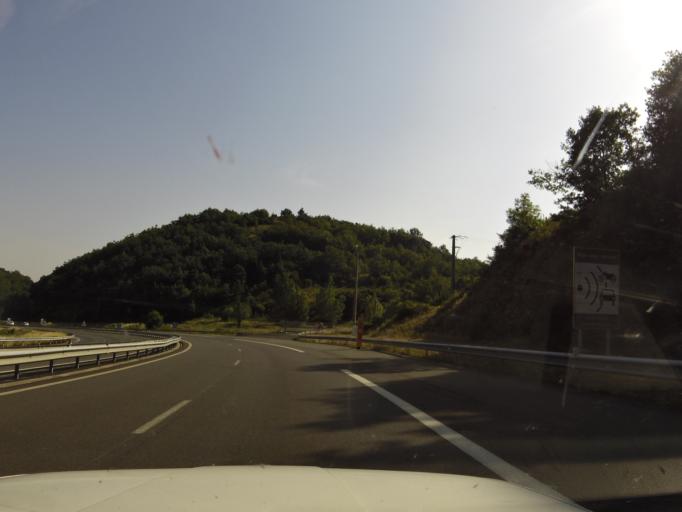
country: FR
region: Languedoc-Roussillon
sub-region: Departement de l'Herault
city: Lodeve
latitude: 43.8364
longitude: 3.3082
